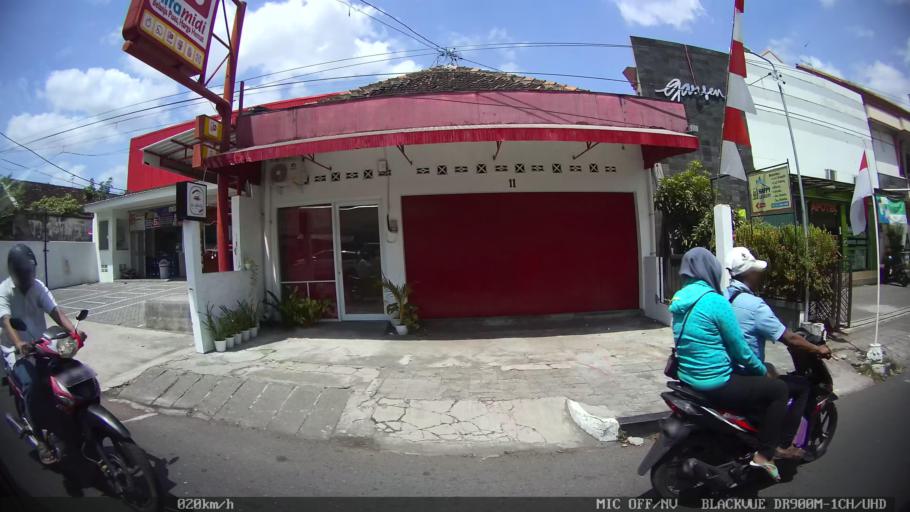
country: ID
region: Daerah Istimewa Yogyakarta
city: Yogyakarta
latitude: -7.8084
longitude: 110.3548
